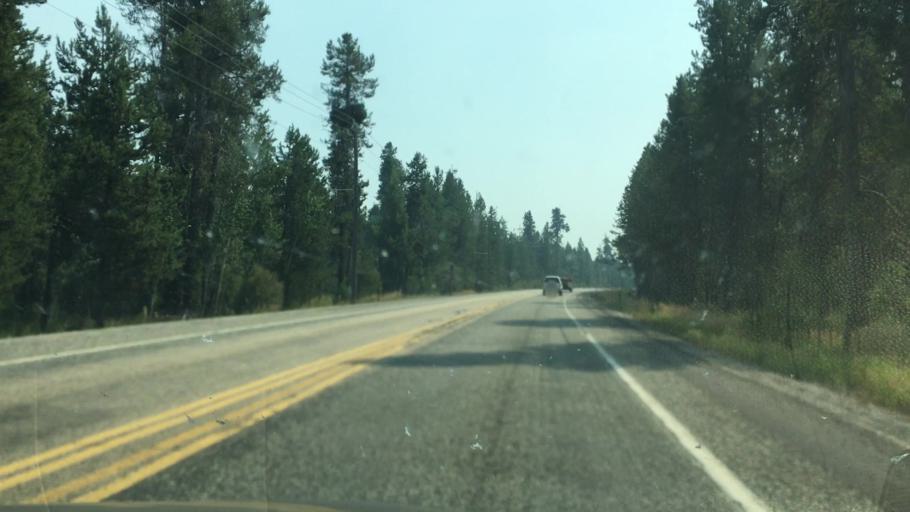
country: US
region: Idaho
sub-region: Valley County
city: Cascade
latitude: 44.4049
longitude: -116.0001
